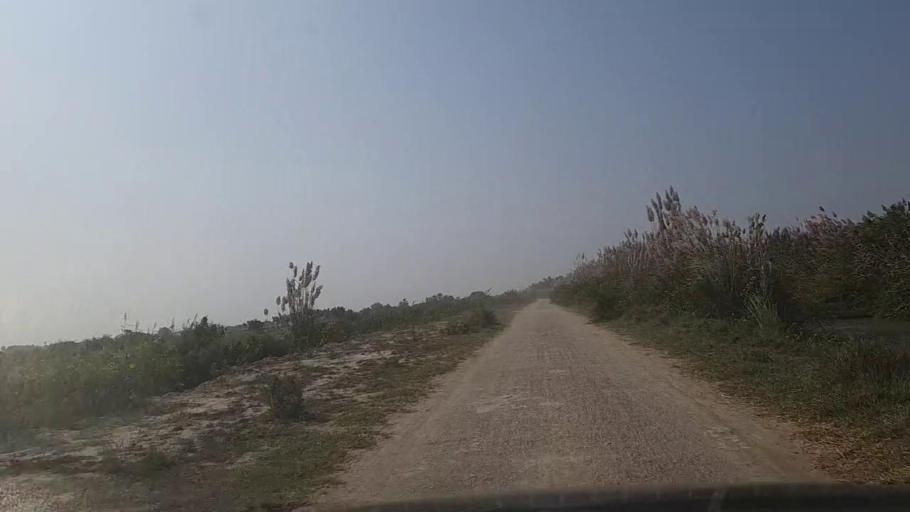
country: PK
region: Sindh
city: Gharo
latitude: 24.7087
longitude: 67.6502
